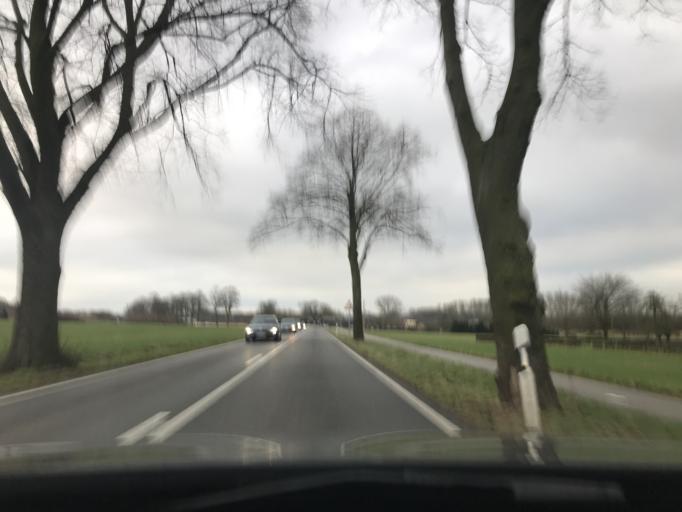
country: DE
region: North Rhine-Westphalia
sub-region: Regierungsbezirk Dusseldorf
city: Uedem
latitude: 51.6490
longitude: 6.2777
